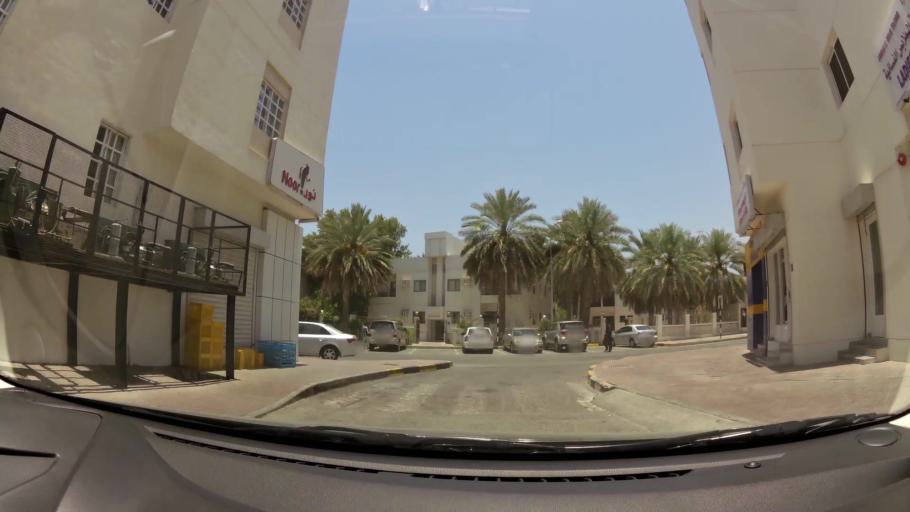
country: OM
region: Muhafazat Masqat
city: Muscat
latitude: 23.6166
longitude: 58.5406
